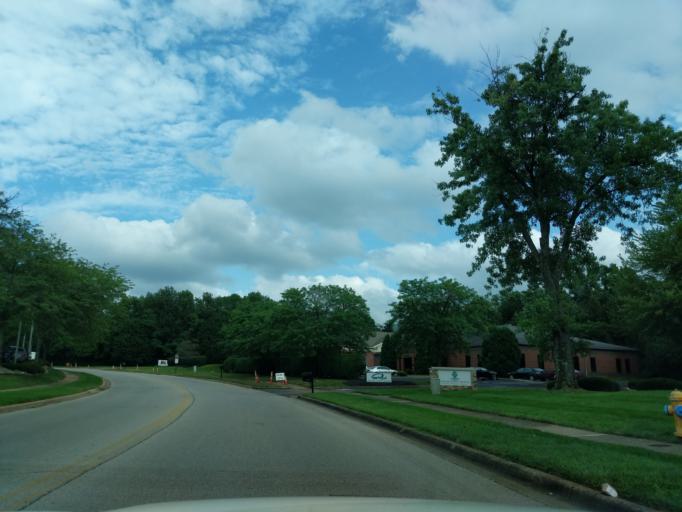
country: US
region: Kentucky
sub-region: Jefferson County
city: Hurstbourne Acres
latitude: 38.2162
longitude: -85.5816
